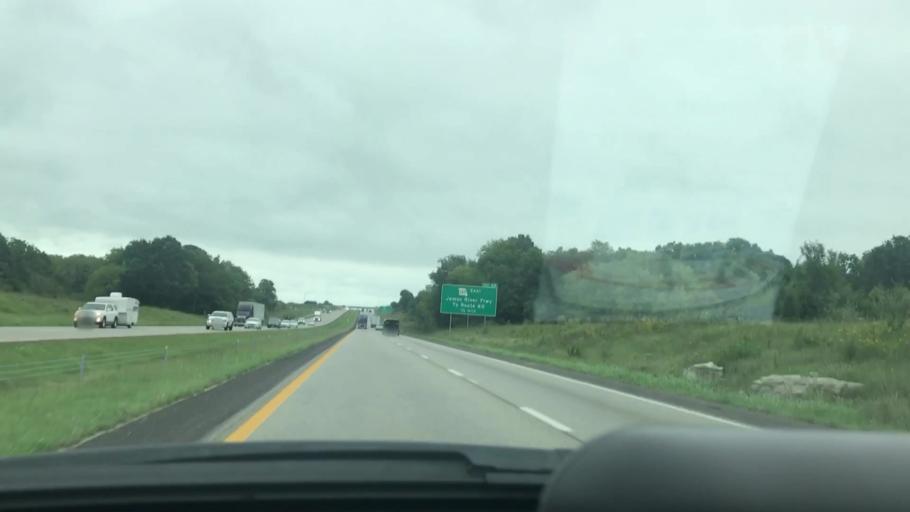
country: US
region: Missouri
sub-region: Greene County
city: Republic
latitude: 37.1931
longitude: -93.4582
